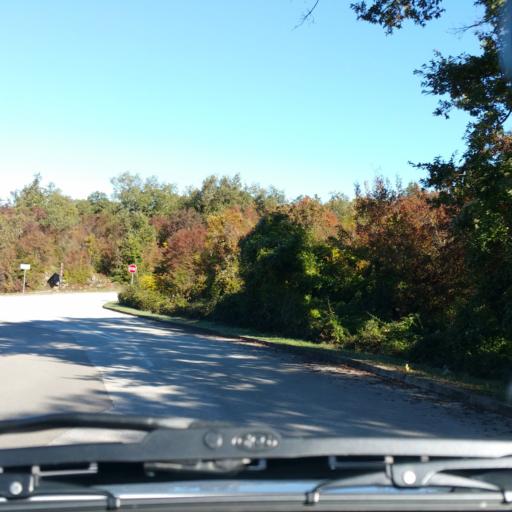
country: HR
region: Primorsko-Goranska
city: Njivice
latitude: 45.1540
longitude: 14.5410
